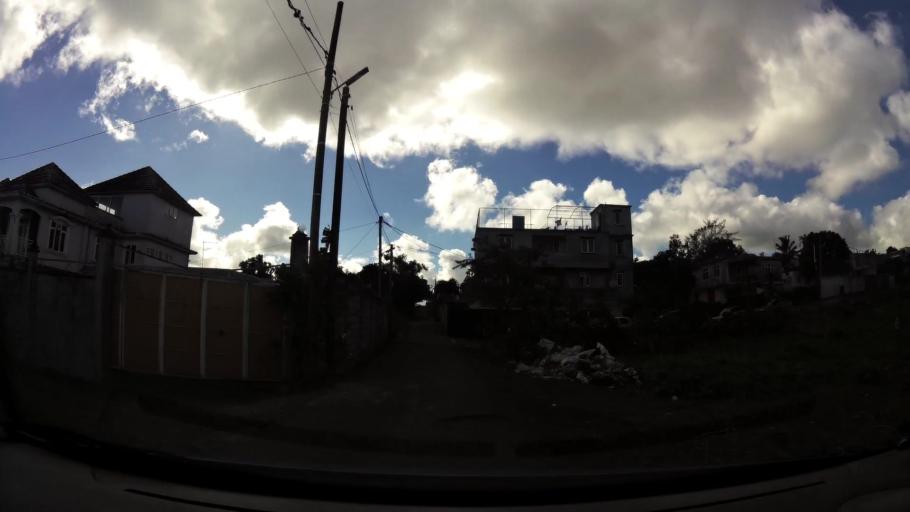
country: MU
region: Plaines Wilhems
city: Curepipe
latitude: -20.3000
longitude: 57.5129
